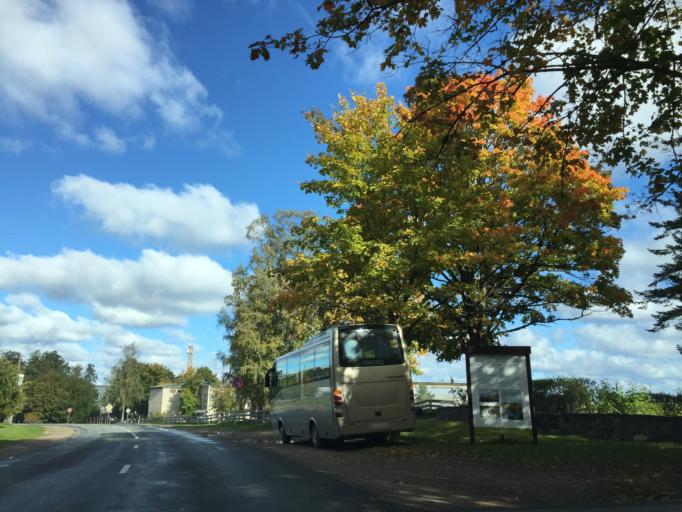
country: LV
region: Tukuma Rajons
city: Engure
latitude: 57.1598
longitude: 23.2298
